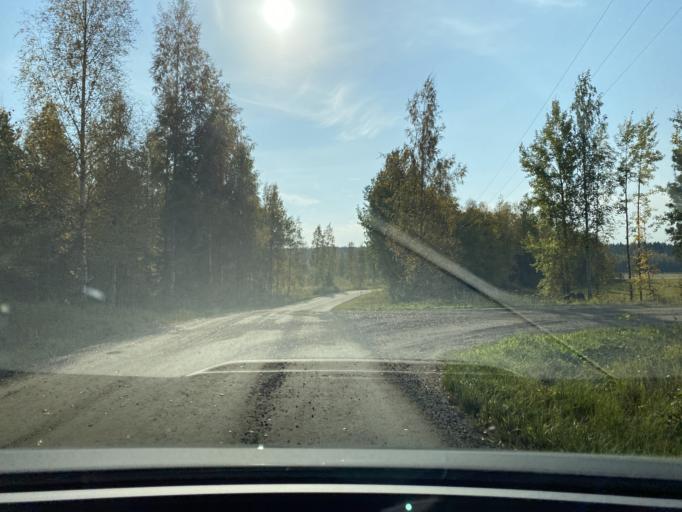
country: FI
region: Pirkanmaa
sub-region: Lounais-Pirkanmaa
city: Punkalaidun
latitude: 61.1117
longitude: 23.2745
